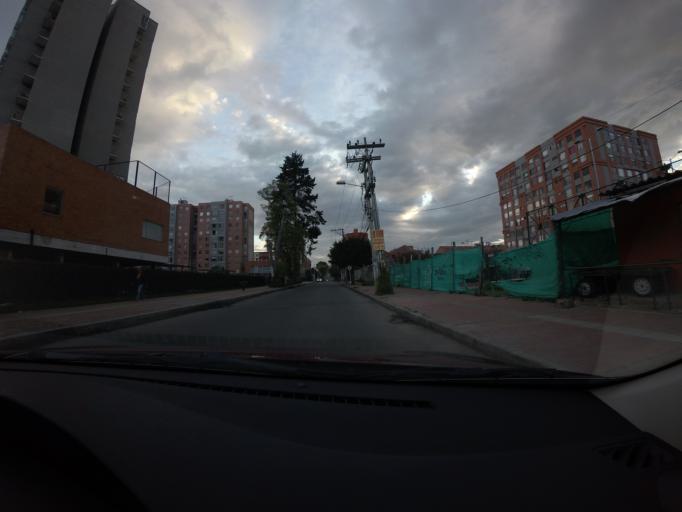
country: CO
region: Cundinamarca
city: Cota
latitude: 4.7597
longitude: -74.0416
